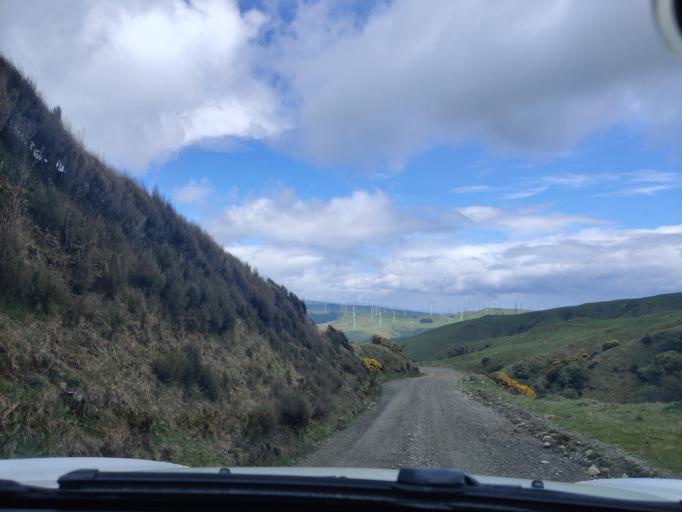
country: NZ
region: Manawatu-Wanganui
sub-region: Palmerston North City
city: Palmerston North
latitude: -40.2758
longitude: 175.8528
